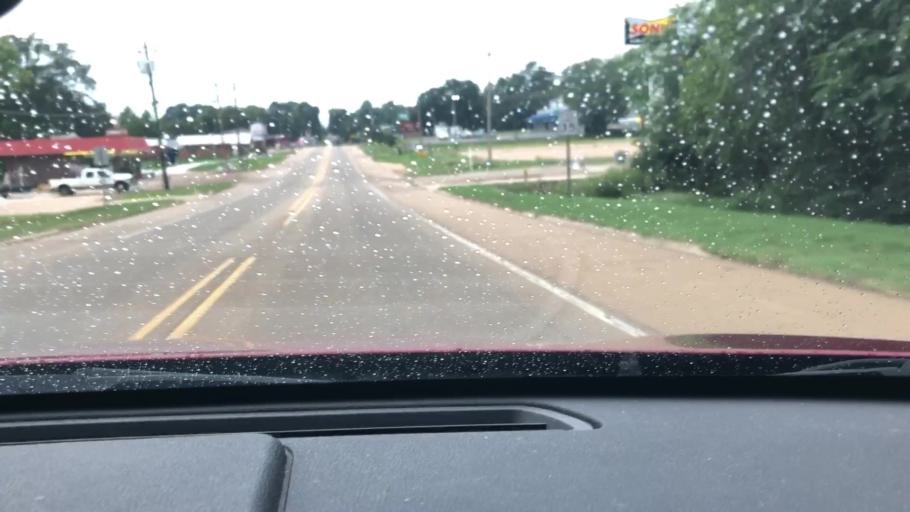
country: US
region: Arkansas
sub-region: Lafayette County
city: Stamps
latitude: 33.3652
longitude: -93.4844
